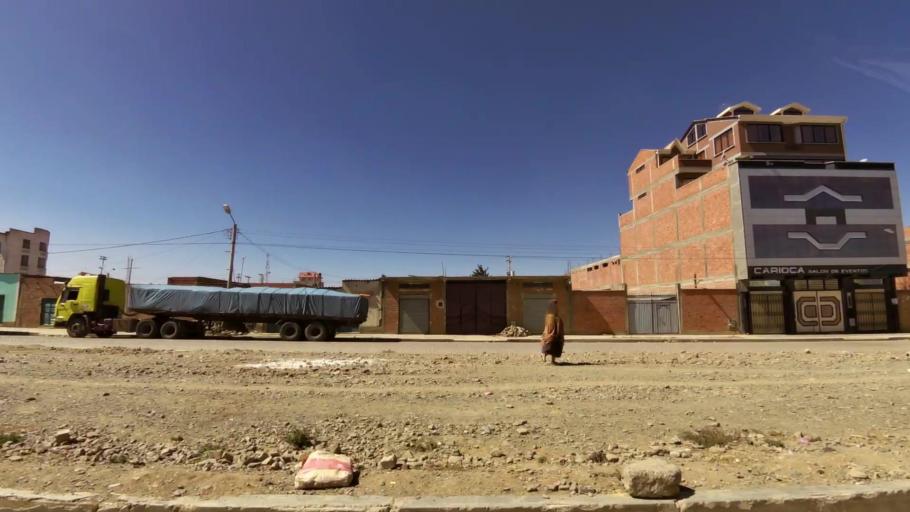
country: BO
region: La Paz
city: La Paz
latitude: -16.5368
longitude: -68.1939
